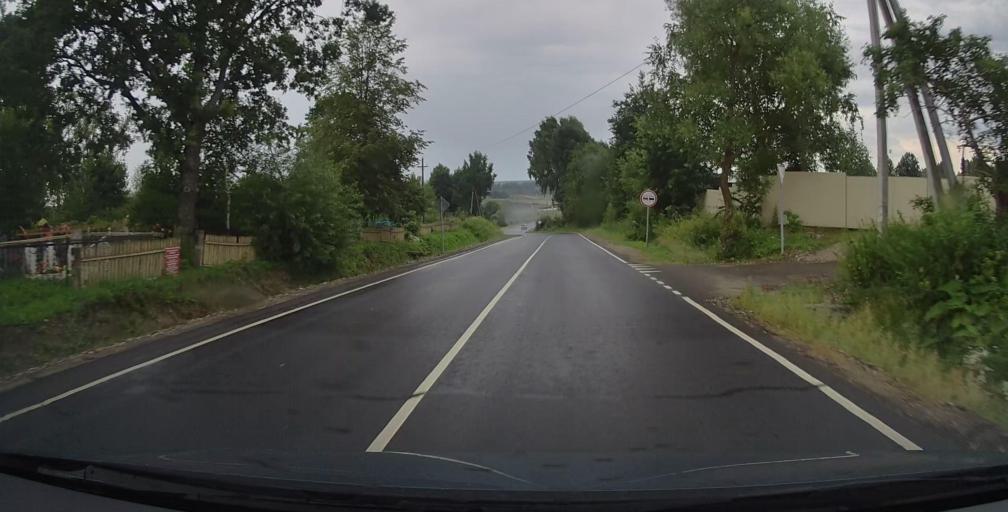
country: RU
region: Jaroslavl
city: Uglich
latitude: 57.5511
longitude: 38.2815
